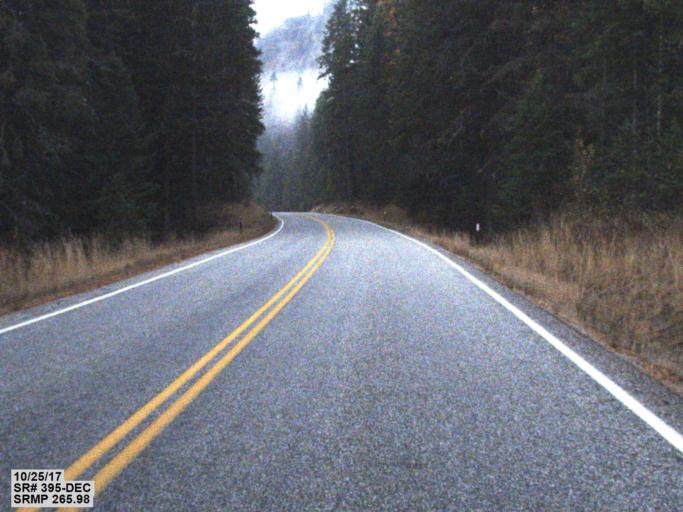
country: CA
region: British Columbia
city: Grand Forks
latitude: 48.9410
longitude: -118.2221
